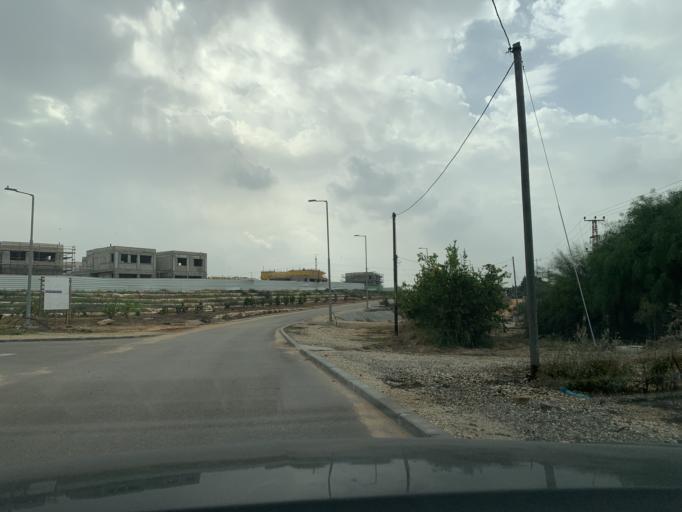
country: IL
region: Central District
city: Tirah
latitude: 32.2180
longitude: 34.9346
